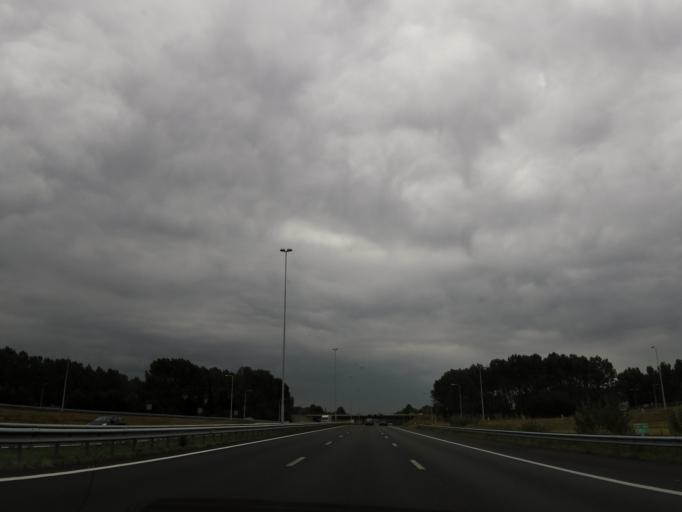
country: NL
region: North Brabant
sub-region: Gemeente Best
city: Best
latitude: 51.5246
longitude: 5.3923
